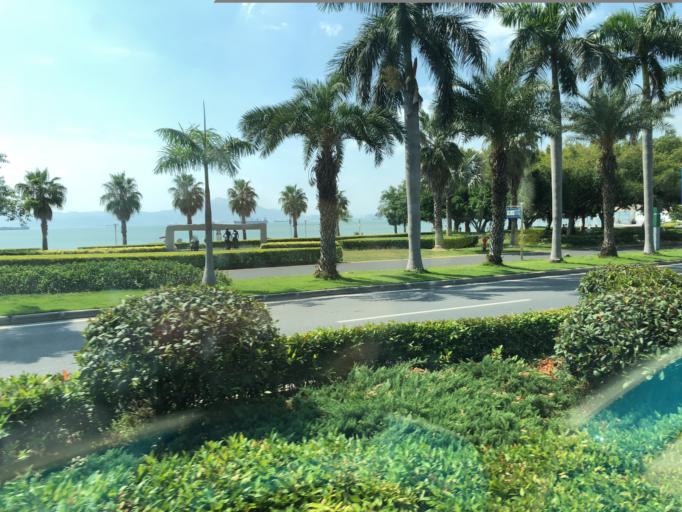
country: CN
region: Fujian
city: Xiamen
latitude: 24.4267
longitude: 118.1264
